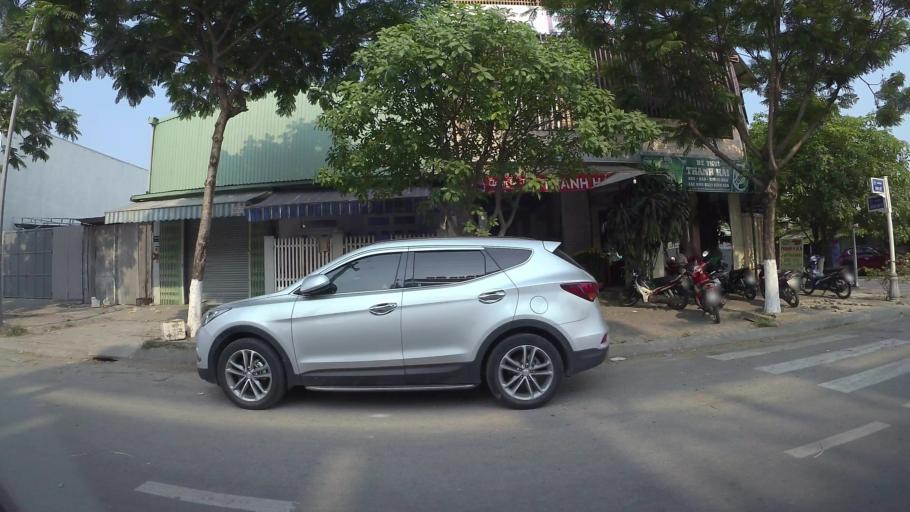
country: VN
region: Da Nang
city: Thanh Khe
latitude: 16.0494
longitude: 108.1745
